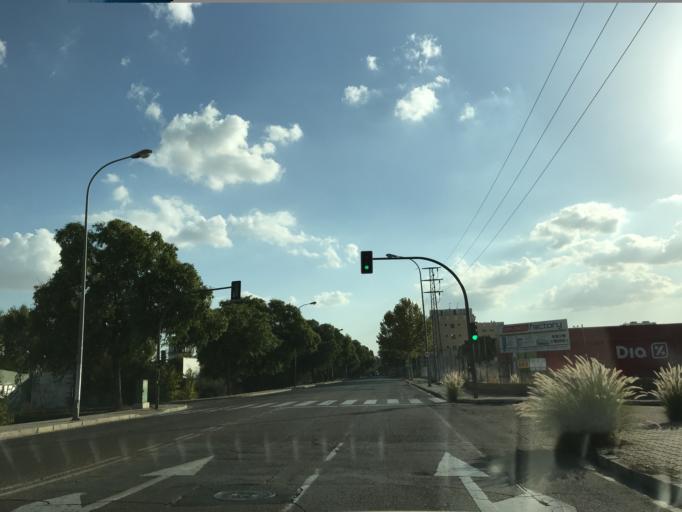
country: ES
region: Andalusia
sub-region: Provincia de Sevilla
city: Sevilla
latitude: 37.4113
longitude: -5.9325
